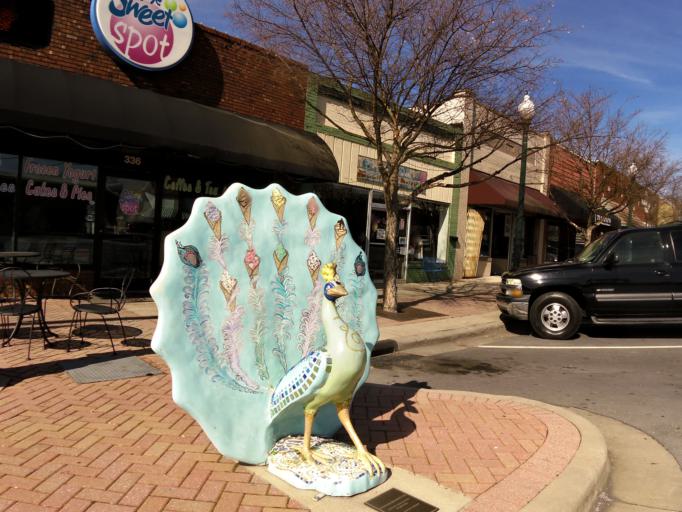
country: US
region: Georgia
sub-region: Whitfield County
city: Dalton
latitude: 34.7687
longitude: -84.9680
